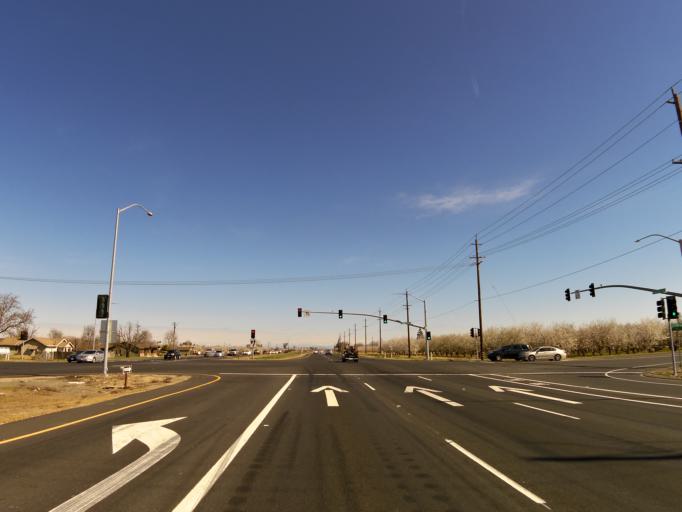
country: US
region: California
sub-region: Stanislaus County
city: Del Rio
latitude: 37.7110
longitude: -121.0228
